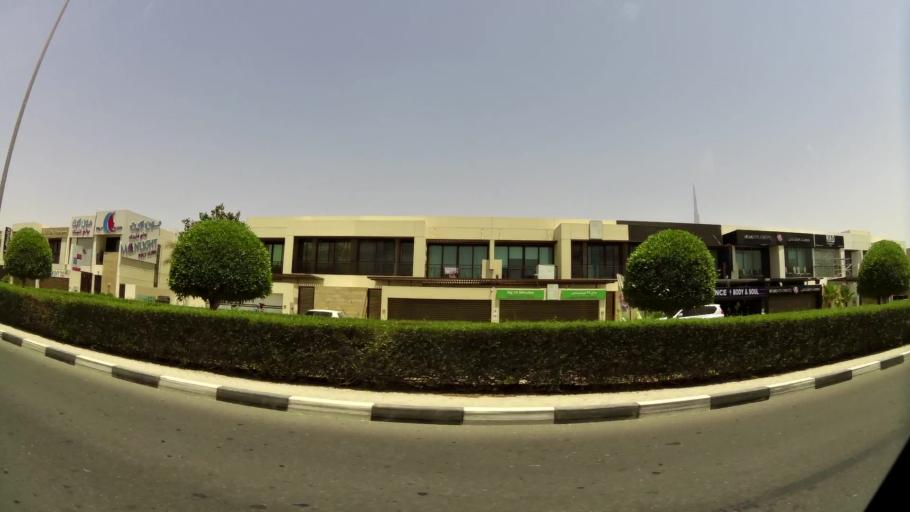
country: AE
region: Dubai
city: Dubai
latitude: 25.2180
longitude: 55.2612
